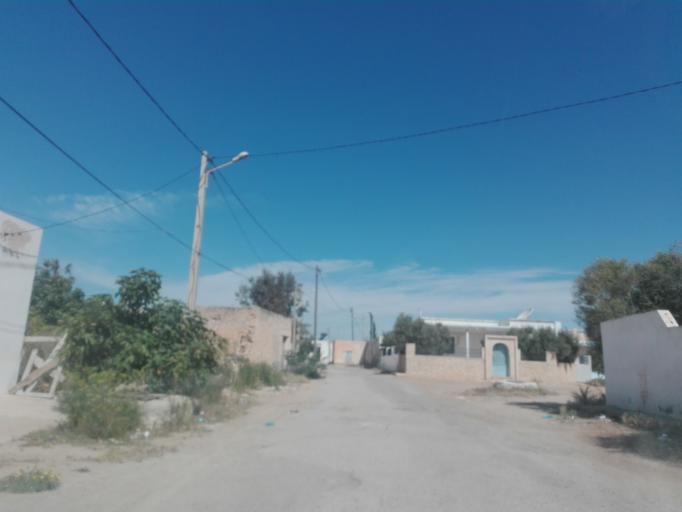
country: TN
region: Safaqis
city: Al Qarmadah
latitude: 34.6724
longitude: 11.1387
